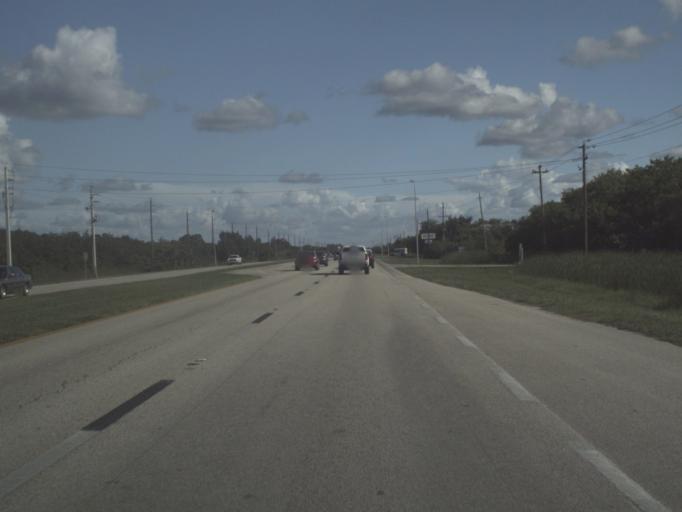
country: US
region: Florida
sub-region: Charlotte County
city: Charlotte Park
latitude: 26.9072
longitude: -82.0391
